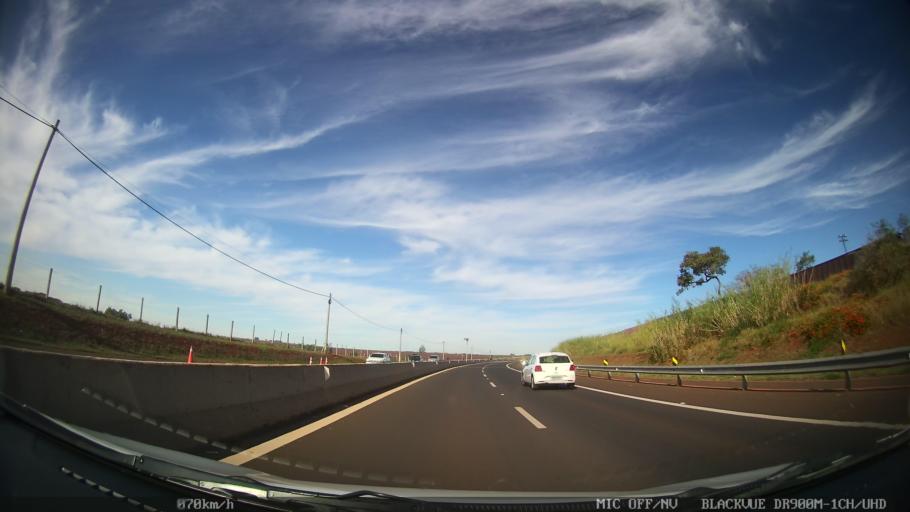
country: BR
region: Sao Paulo
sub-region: Araraquara
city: Araraquara
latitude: -21.7907
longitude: -48.1363
